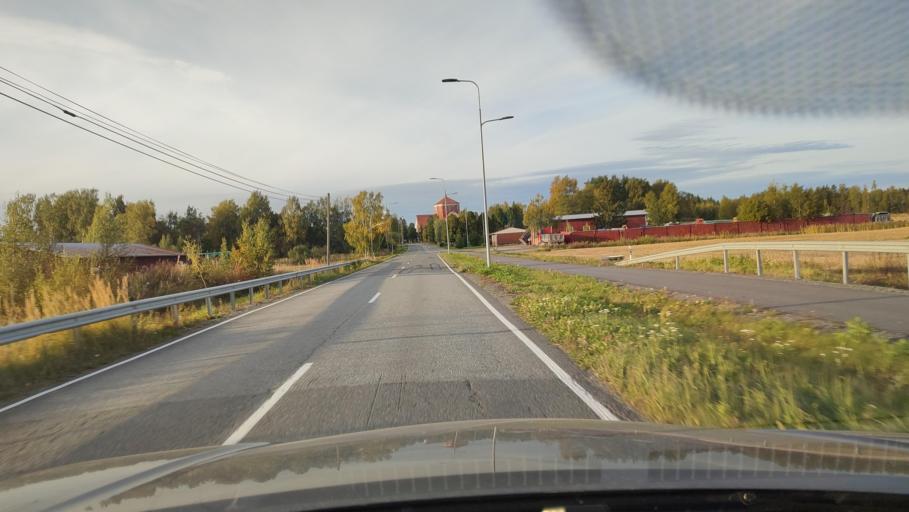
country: FI
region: Ostrobothnia
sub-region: Sydosterbotten
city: Kristinestad
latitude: 62.2421
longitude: 21.5210
